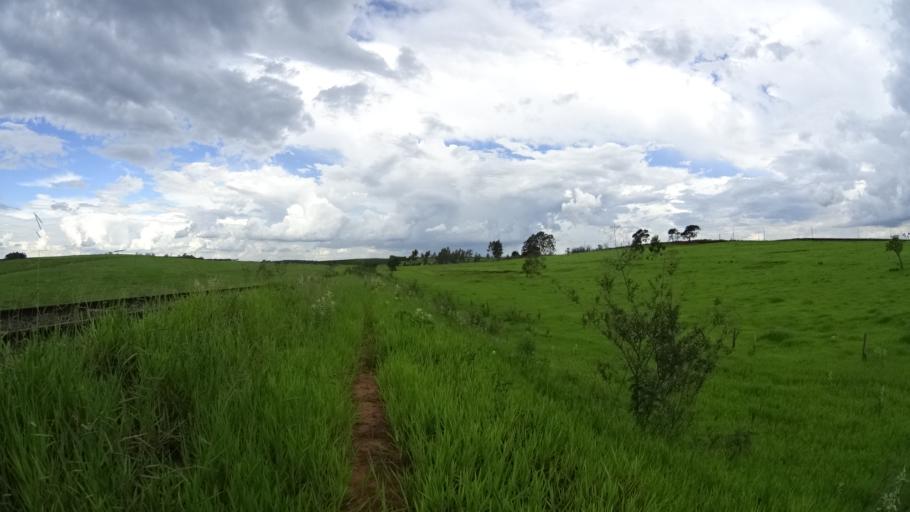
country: BR
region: Sao Paulo
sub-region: Marilia
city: Marilia
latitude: -22.2169
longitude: -49.8694
